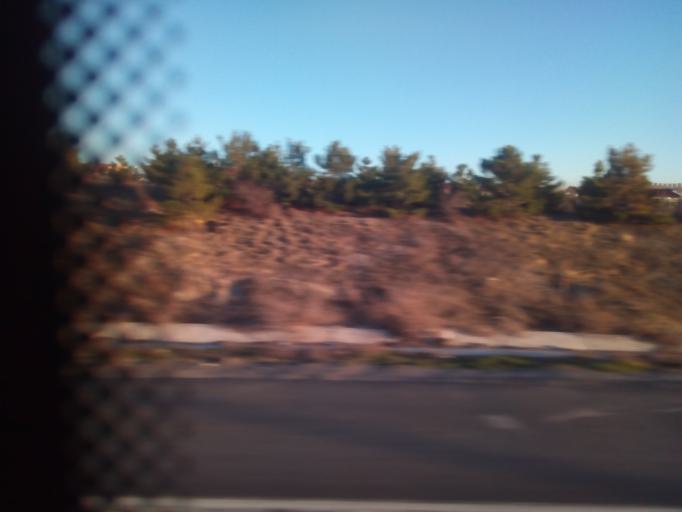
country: TR
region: Ankara
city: Etimesgut
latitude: 39.8968
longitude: 32.6202
